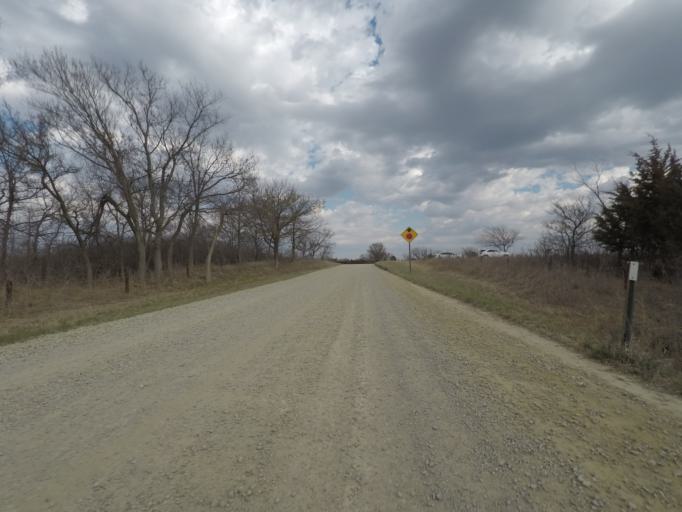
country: US
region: Kansas
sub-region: Riley County
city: Manhattan
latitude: 39.2226
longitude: -96.6216
